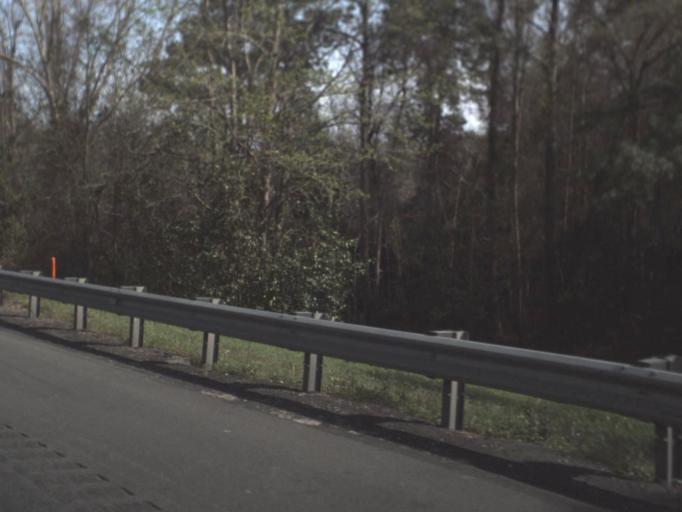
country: US
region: Florida
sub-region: Leon County
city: Tallahassee
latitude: 30.5015
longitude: -84.2352
